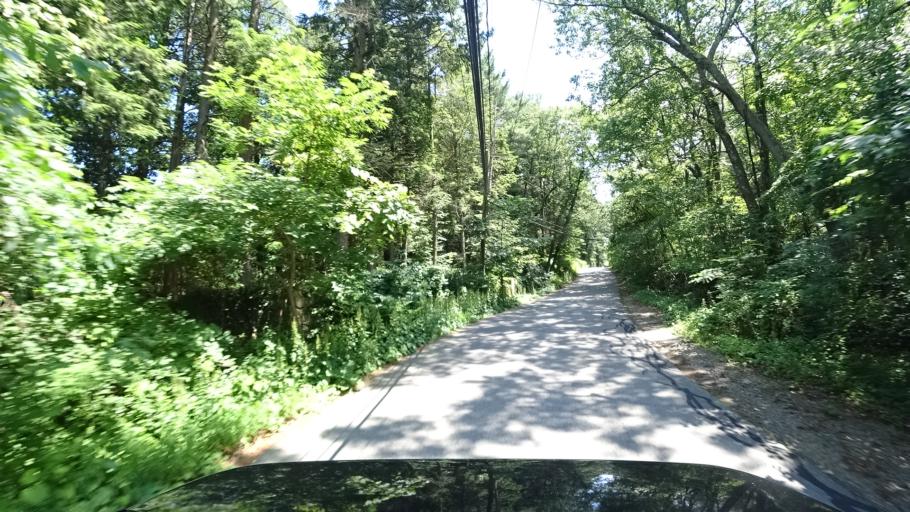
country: US
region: Massachusetts
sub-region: Norfolk County
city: Dedham
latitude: 42.2532
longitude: -71.1959
